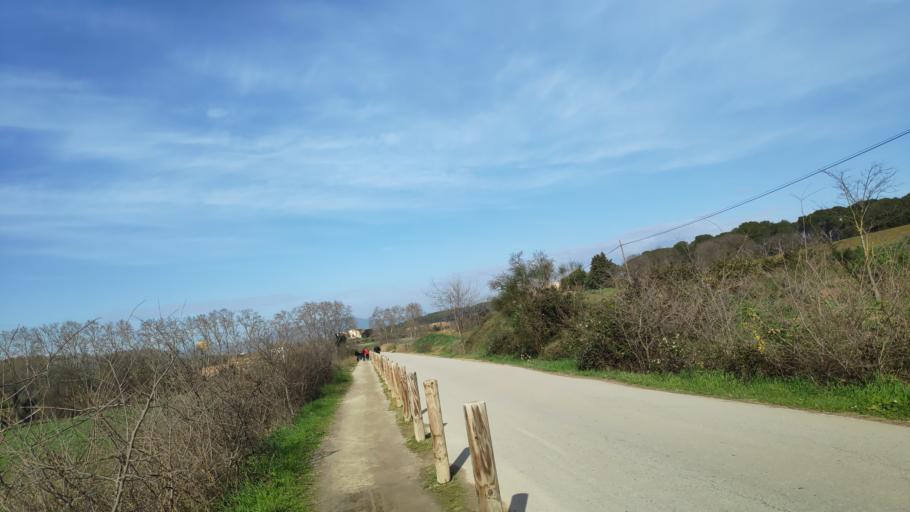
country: ES
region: Catalonia
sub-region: Provincia de Barcelona
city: Mollet del Valles
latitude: 41.5580
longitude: 2.2027
